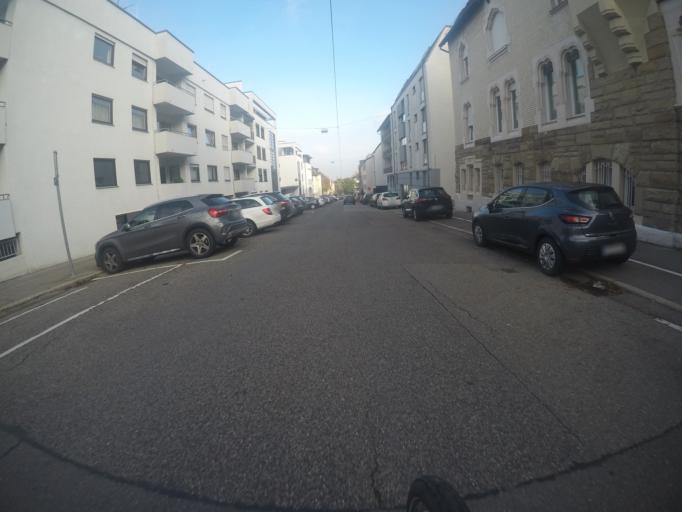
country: DE
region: Baden-Wuerttemberg
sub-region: Regierungsbezirk Stuttgart
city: Stuttgart
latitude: 48.7682
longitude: 9.1830
